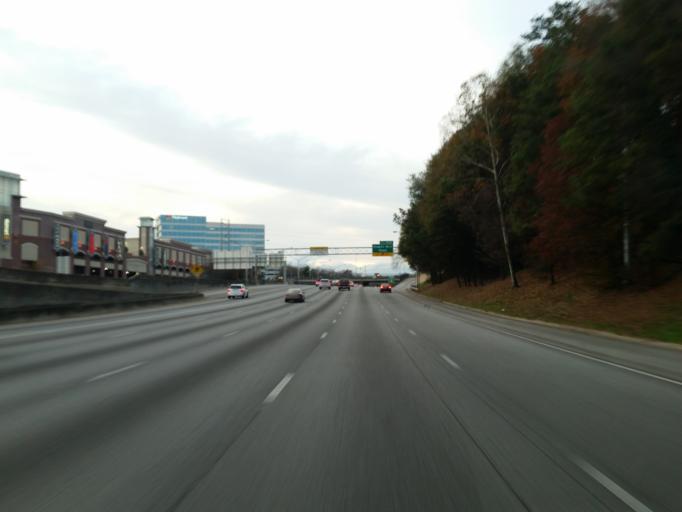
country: US
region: Georgia
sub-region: Fulton County
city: Atlanta
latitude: 33.8036
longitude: -84.4090
